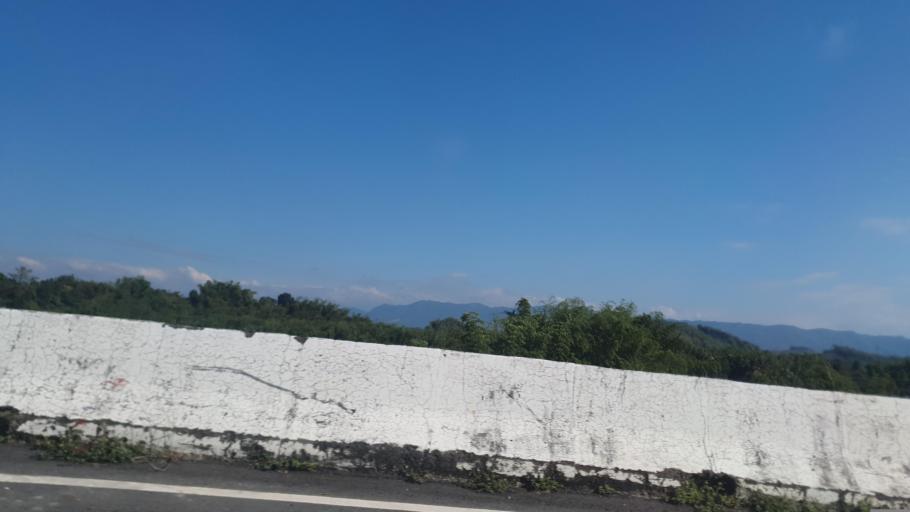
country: TW
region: Taiwan
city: Yujing
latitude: 23.0499
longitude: 120.4019
